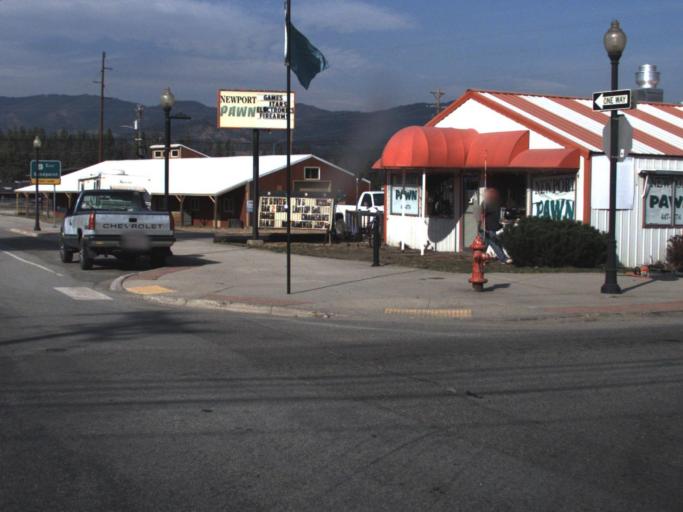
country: US
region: Washington
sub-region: Pend Oreille County
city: Newport
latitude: 48.1822
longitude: -117.0425
